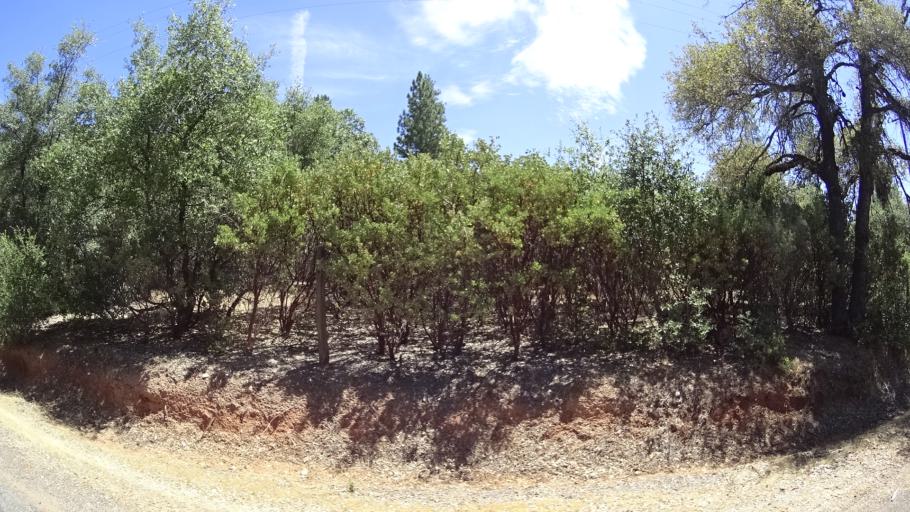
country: US
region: California
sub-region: Calaveras County
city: Murphys
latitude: 38.1759
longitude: -120.4486
